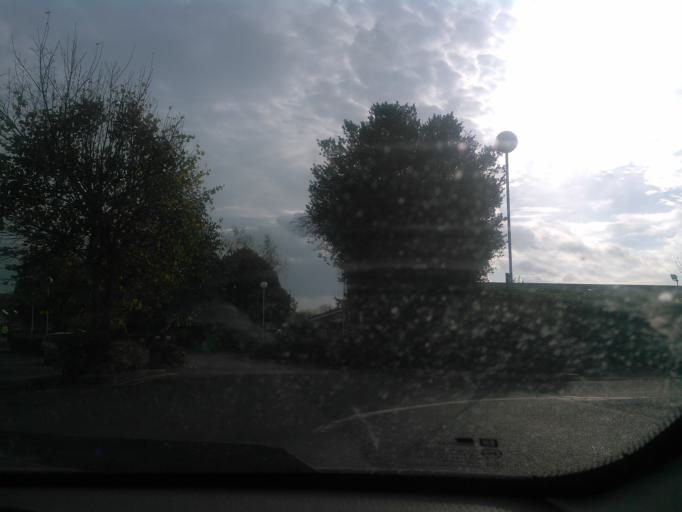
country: GB
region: England
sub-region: Shropshire
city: Wem
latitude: 52.8550
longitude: -2.7228
